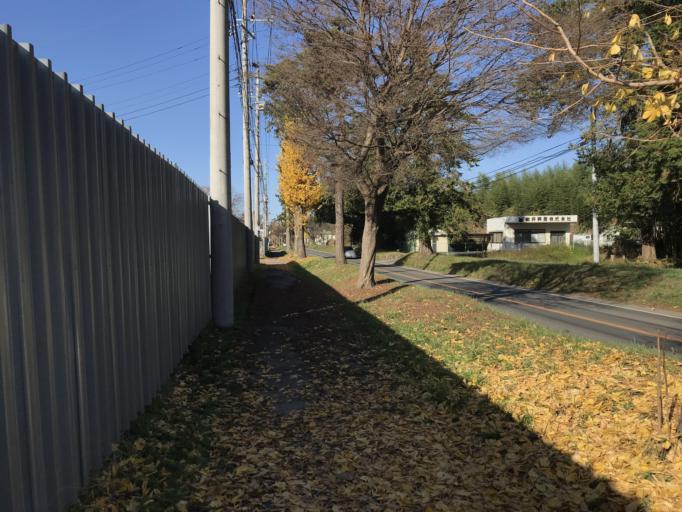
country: JP
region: Tochigi
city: Kanuma
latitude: 36.5957
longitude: 139.7451
